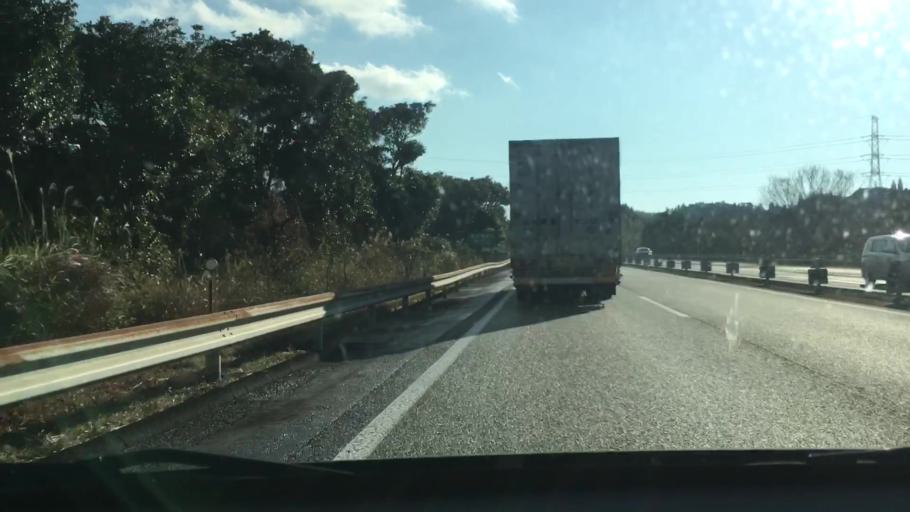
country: JP
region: Kagoshima
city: Okuchi-shinohara
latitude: 31.9334
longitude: 130.7067
